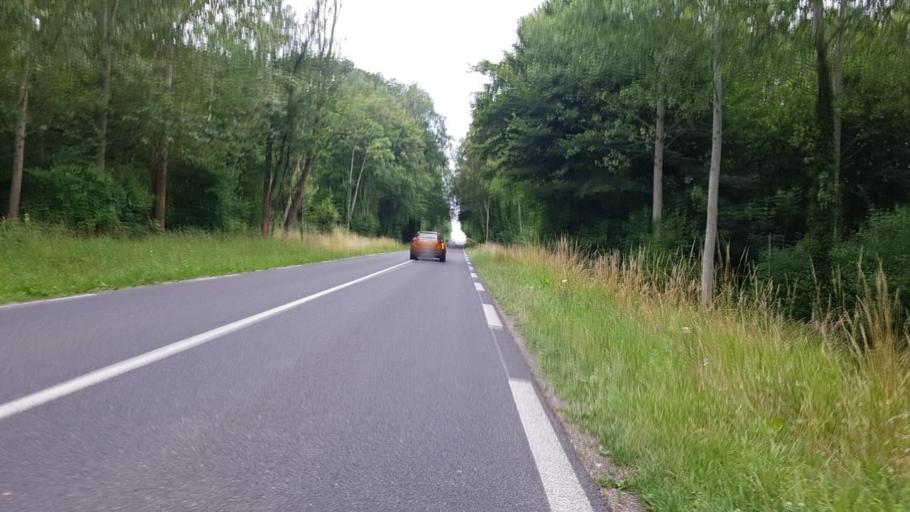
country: FR
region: Champagne-Ardenne
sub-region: Departement de la Marne
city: Sermaize-les-Bains
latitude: 48.7756
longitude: 4.8768
